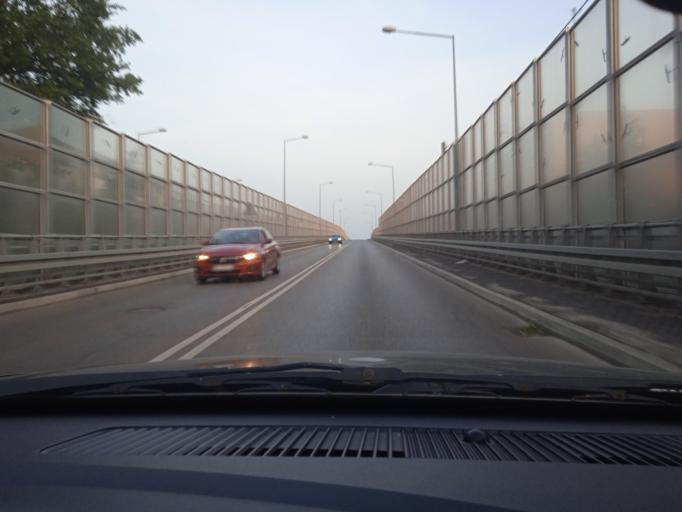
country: PL
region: Masovian Voivodeship
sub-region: Powiat nowodworski
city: Nowy Dwor Mazowiecki
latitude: 52.4271
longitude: 20.7205
